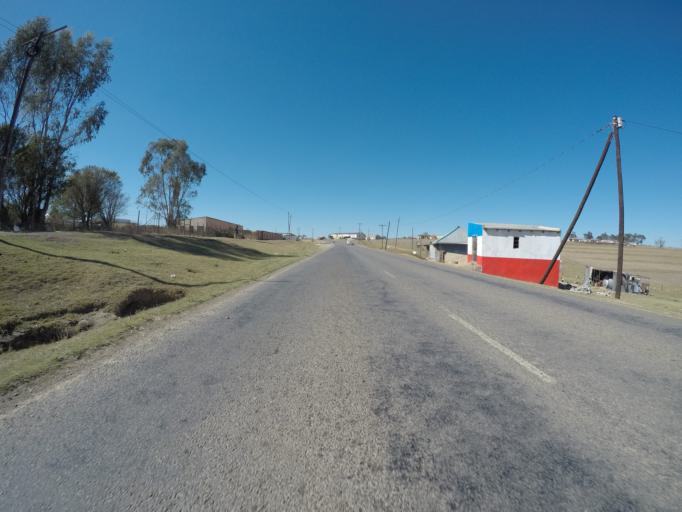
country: ZA
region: Eastern Cape
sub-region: OR Tambo District Municipality
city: Mthatha
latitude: -31.8736
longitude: 28.7534
